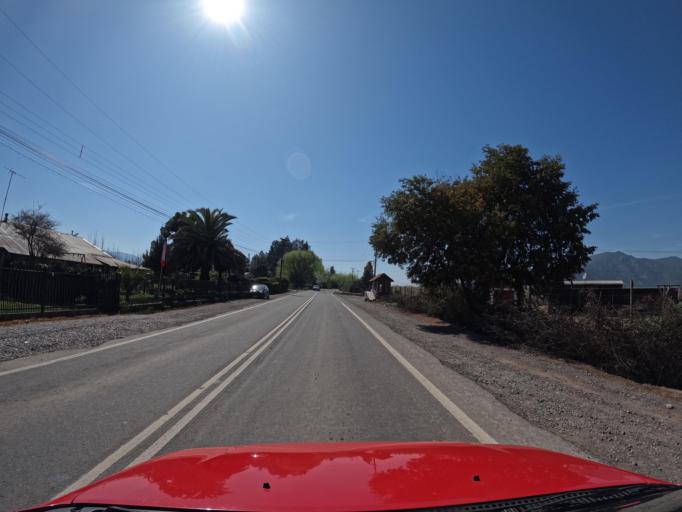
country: CL
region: Maule
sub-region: Provincia de Curico
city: Rauco
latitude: -35.0341
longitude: -71.4456
